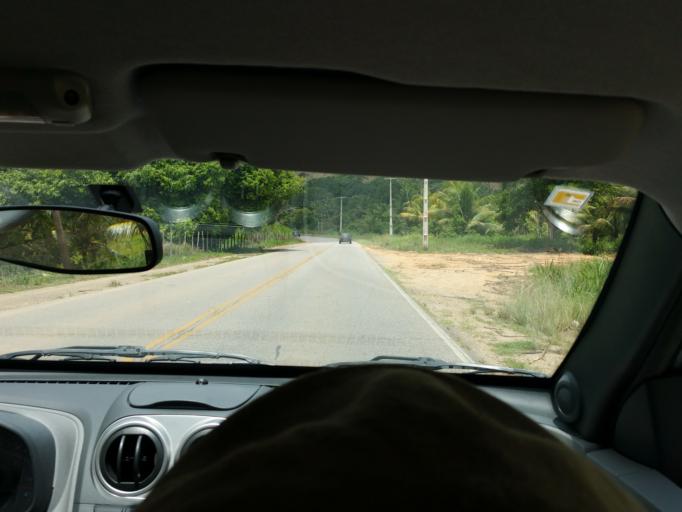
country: BR
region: Pernambuco
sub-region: Sirinhaem
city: Sirinhaem
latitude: -8.6258
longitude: -35.1238
